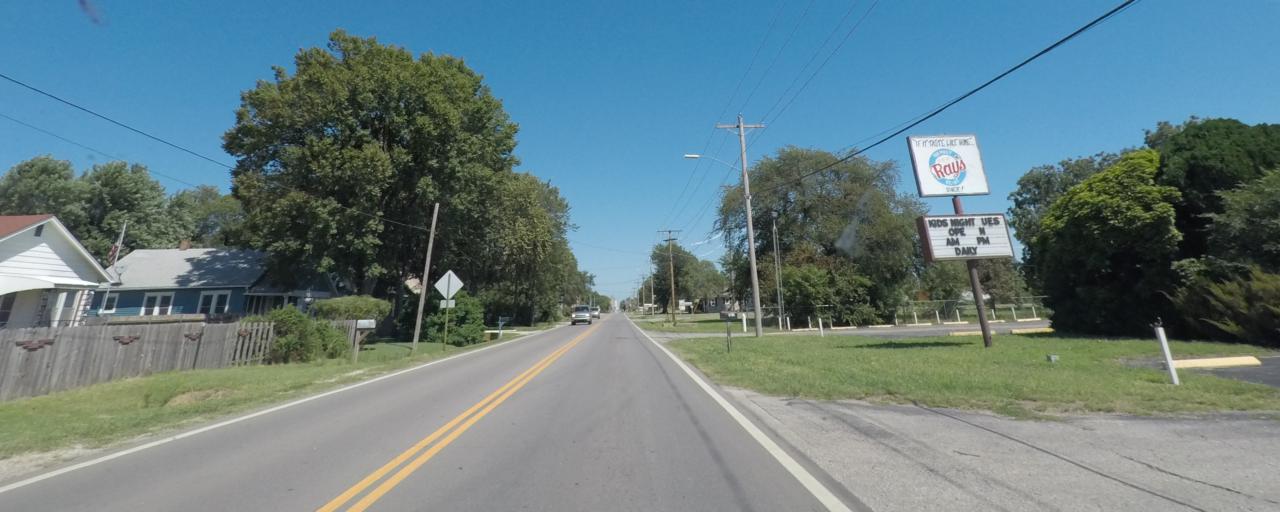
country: US
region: Kansas
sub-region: Sumner County
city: Wellington
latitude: 37.2816
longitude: -97.3943
